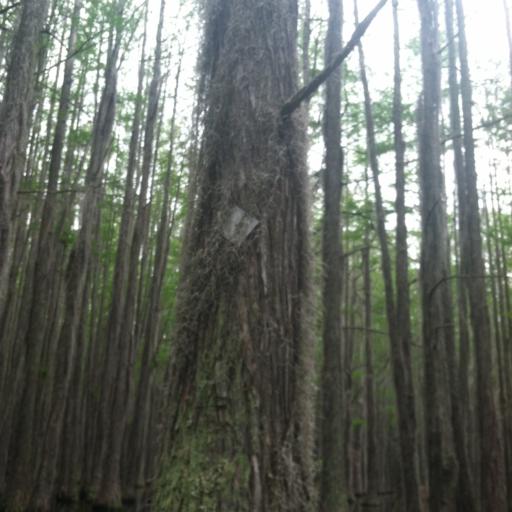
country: US
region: Georgia
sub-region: Emanuel County
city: Twin City
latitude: 32.5560
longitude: -82.1197
